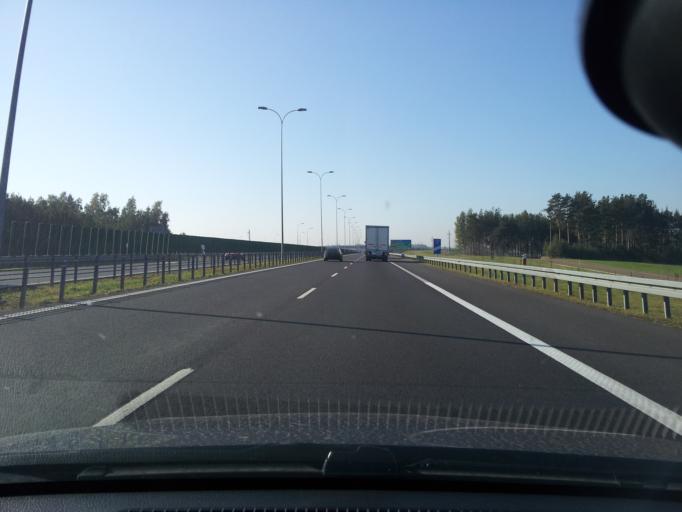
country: PL
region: Kujawsko-Pomorskie
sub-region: Powiat swiecki
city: Warlubie
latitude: 53.6097
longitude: 18.6271
